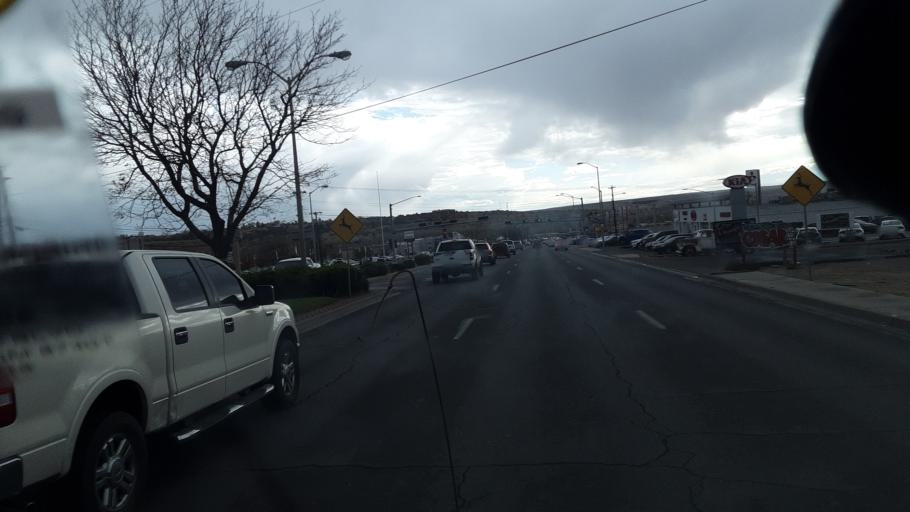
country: US
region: New Mexico
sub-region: San Juan County
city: Farmington
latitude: 36.7576
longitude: -108.1563
